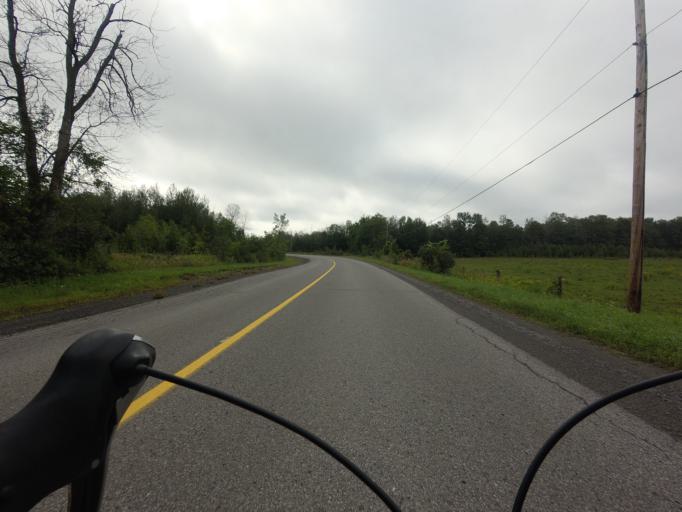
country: CA
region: Ontario
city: Bells Corners
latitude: 45.0696
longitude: -75.7315
